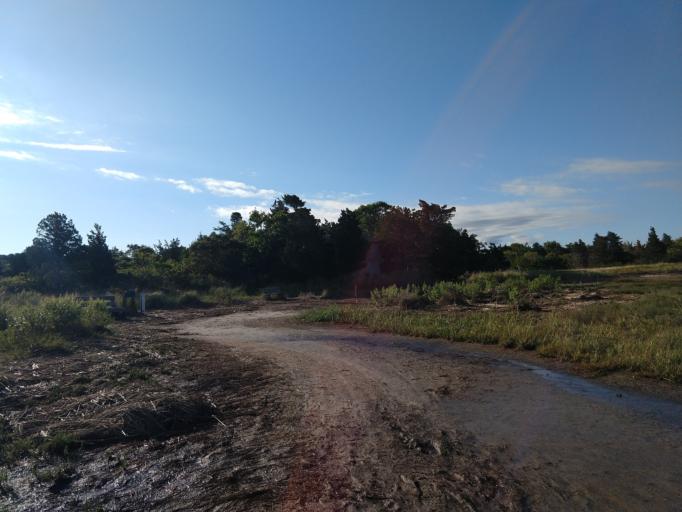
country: US
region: Massachusetts
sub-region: Barnstable County
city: North Eastham
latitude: 41.8808
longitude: -70.0014
